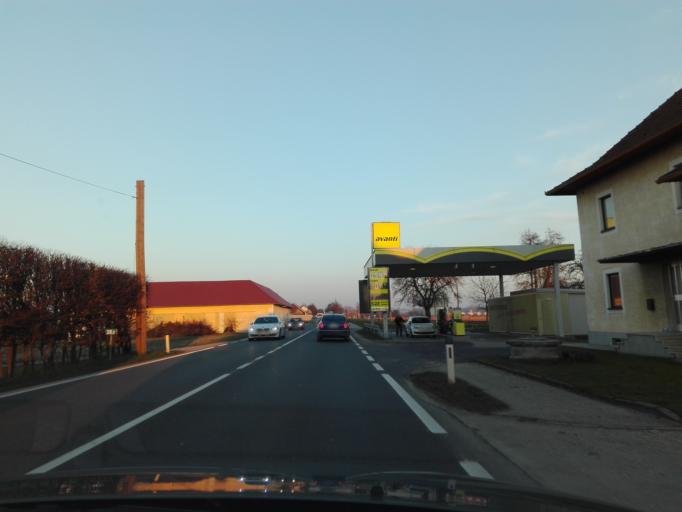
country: AT
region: Upper Austria
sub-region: Politischer Bezirk Urfahr-Umgebung
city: Goldworth
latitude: 48.2881
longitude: 14.0756
